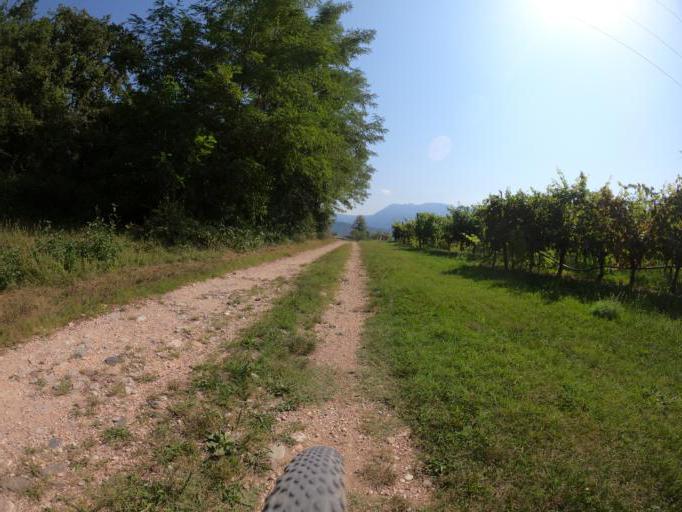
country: IT
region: Veneto
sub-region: Provincia di Verona
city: Caprino Veronese
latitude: 45.5869
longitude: 10.7888
